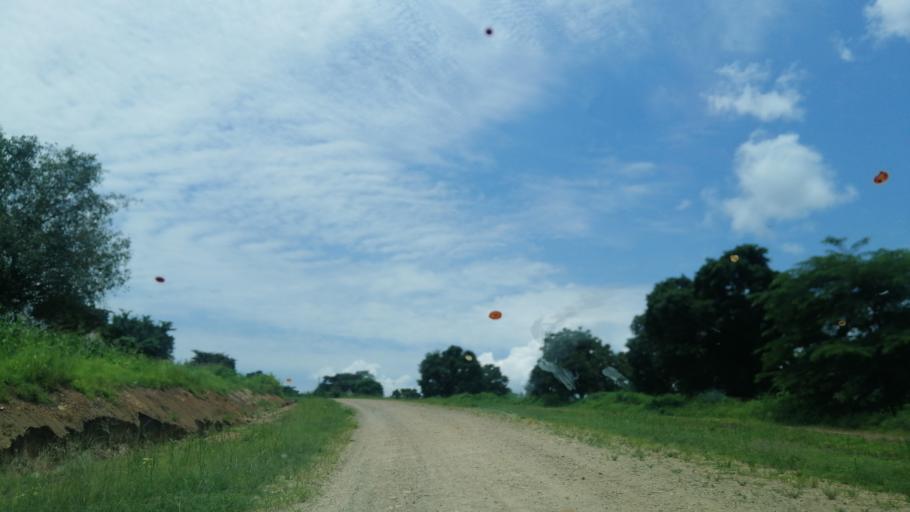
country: ET
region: Oromiya
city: Mendi
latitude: 10.1679
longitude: 35.0927
